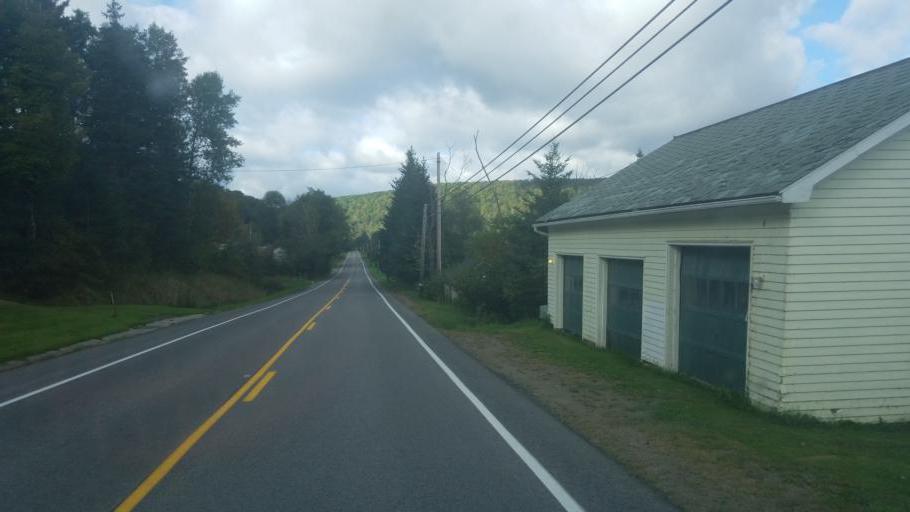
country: US
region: New York
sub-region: Allegany County
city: Cuba
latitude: 42.1439
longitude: -78.3157
